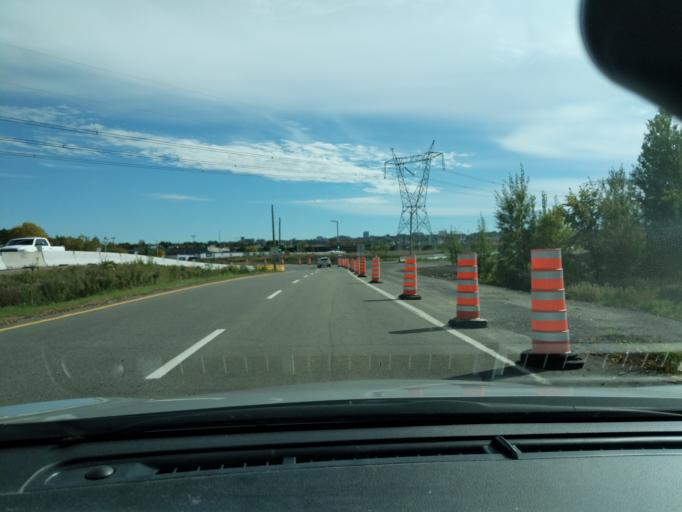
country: CA
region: Quebec
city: L'Ancienne-Lorette
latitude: 46.8020
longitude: -71.3236
